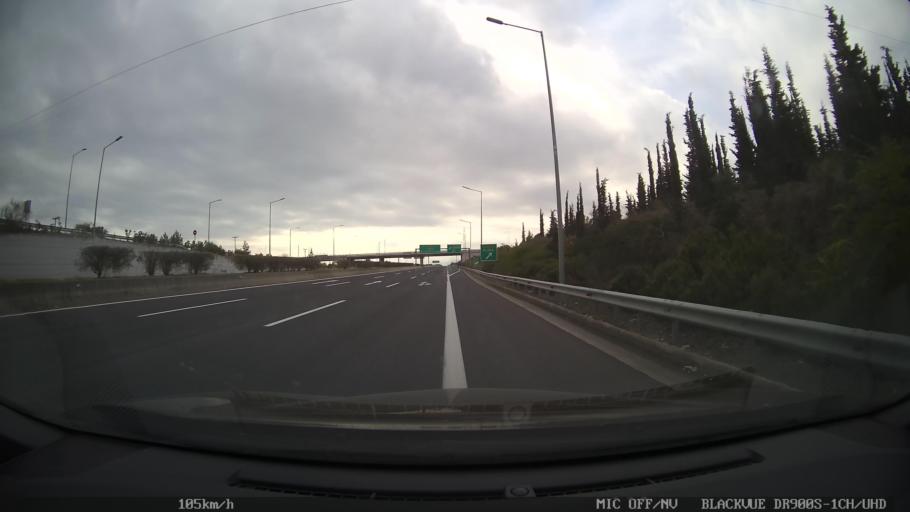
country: GR
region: Central Macedonia
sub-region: Nomos Pierias
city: Litochoro
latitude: 40.1345
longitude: 22.5453
